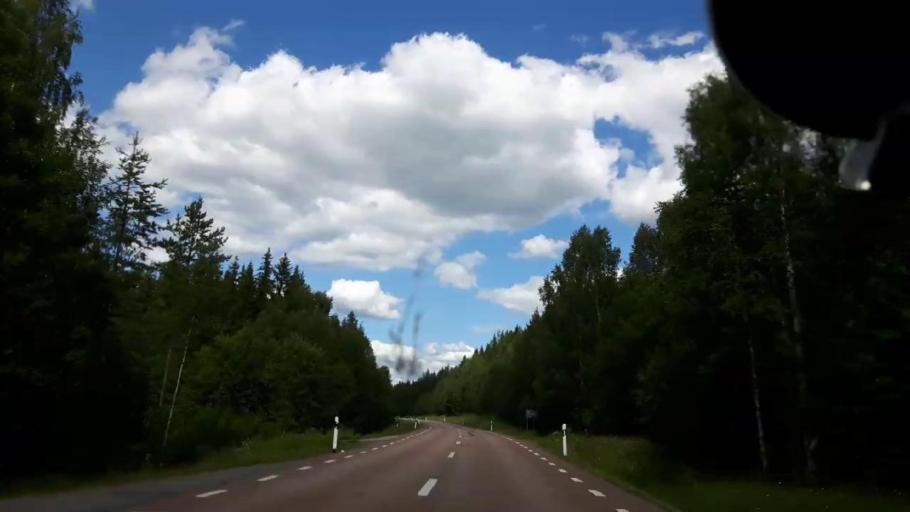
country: SE
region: Jaemtland
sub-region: Ragunda Kommun
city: Hammarstrand
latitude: 62.9201
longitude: 16.7039
